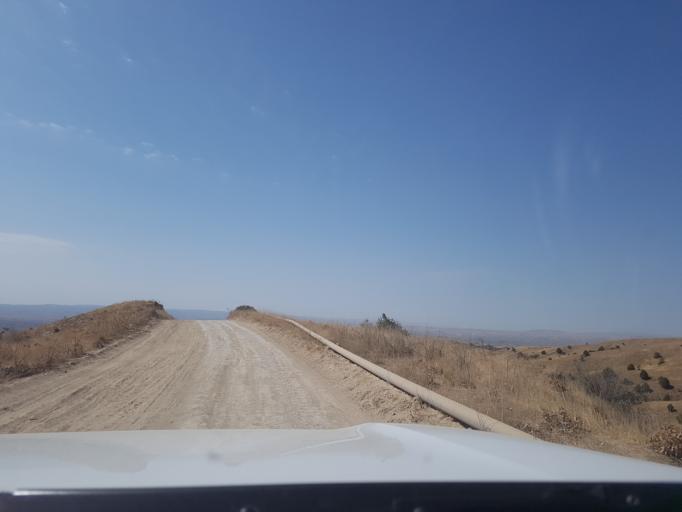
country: TM
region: Ahal
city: Baharly
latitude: 38.2813
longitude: 56.9243
